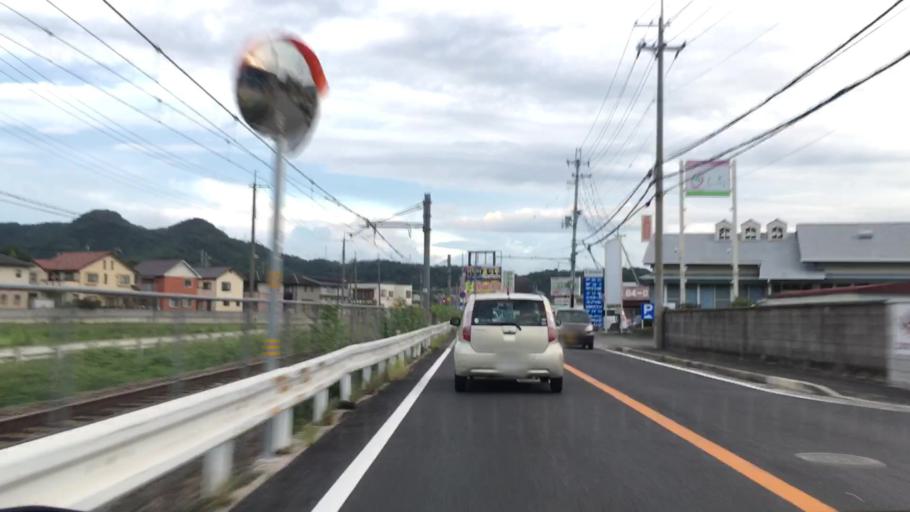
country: JP
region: Hyogo
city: Himeji
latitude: 34.8793
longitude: 134.7288
